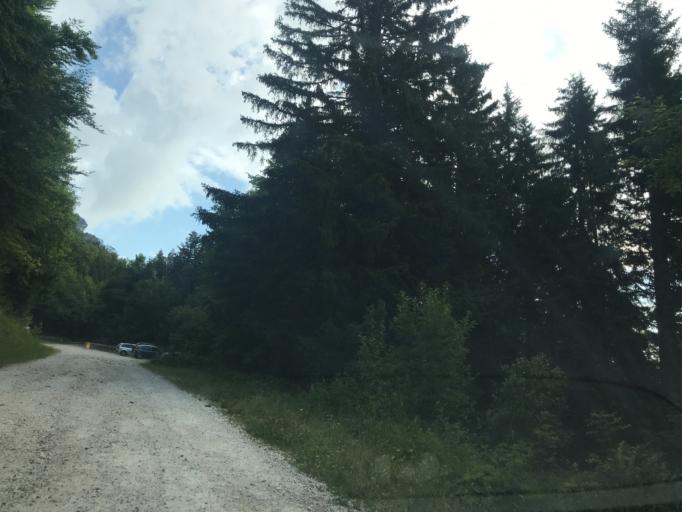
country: FR
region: Rhone-Alpes
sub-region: Departement de l'Isere
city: Barraux
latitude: 45.4200
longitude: 5.9376
